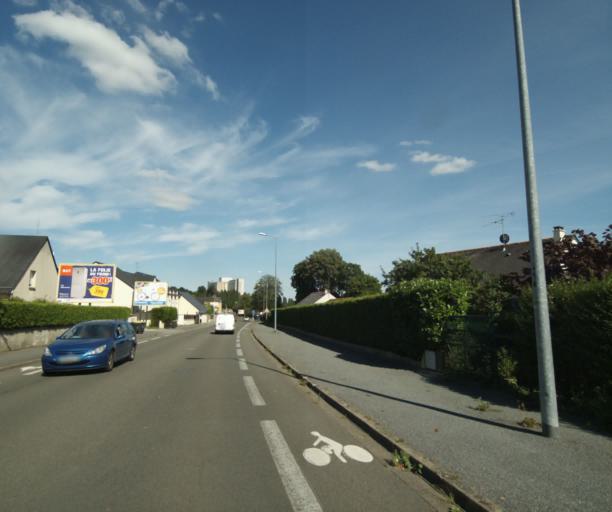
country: FR
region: Pays de la Loire
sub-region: Departement de la Mayenne
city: Laval
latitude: 48.0651
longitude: -0.7925
